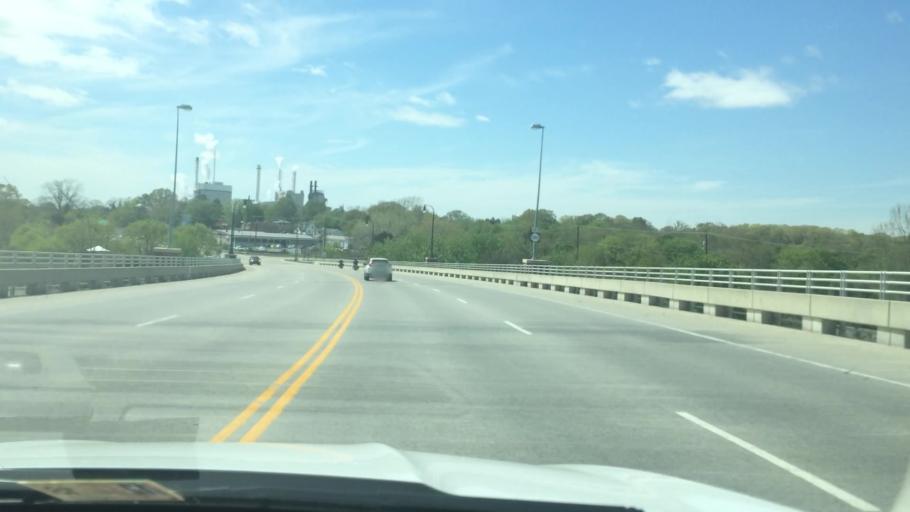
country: US
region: Virginia
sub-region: King William County
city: West Point
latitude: 37.5382
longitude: -76.7919
